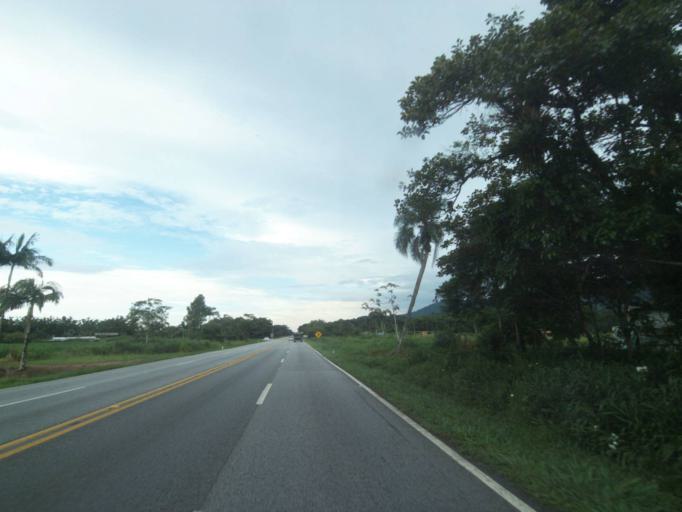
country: BR
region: Parana
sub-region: Pontal Do Parana
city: Pontal do Parana
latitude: -25.6437
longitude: -48.5905
